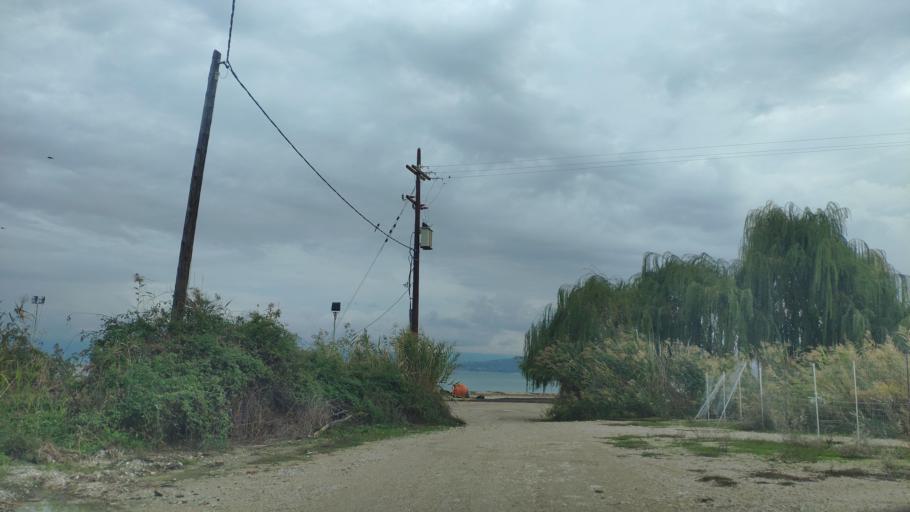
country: GR
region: West Greece
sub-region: Nomos Aitolias kai Akarnanias
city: Monastirakion
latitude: 38.9259
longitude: 21.0236
